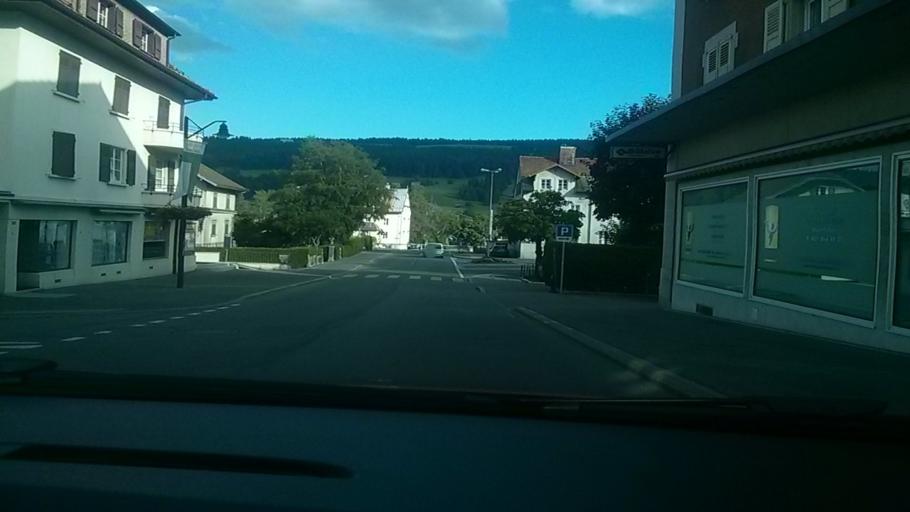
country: CH
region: Vaud
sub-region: Jura-Nord vaudois District
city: Le Chenit
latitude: 46.6069
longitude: 6.2310
